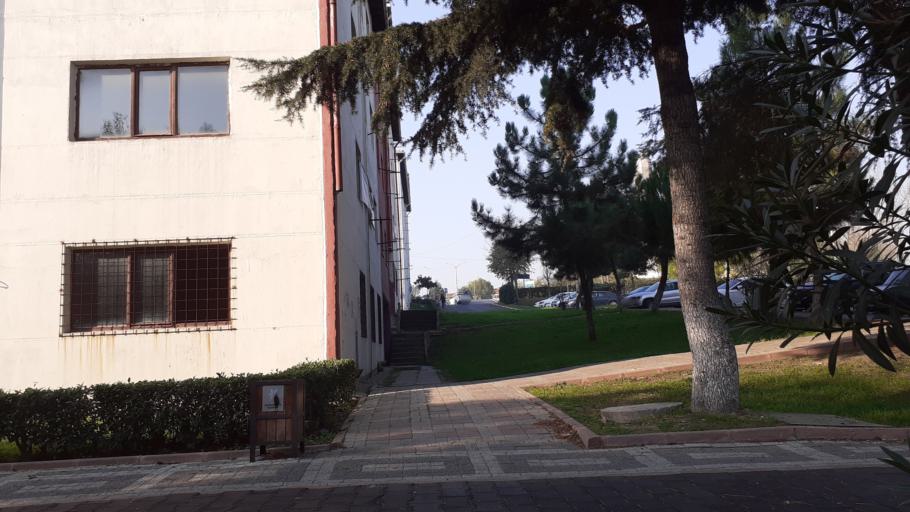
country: TR
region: Istanbul
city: Mahmutbey
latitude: 41.0489
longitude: 28.7956
